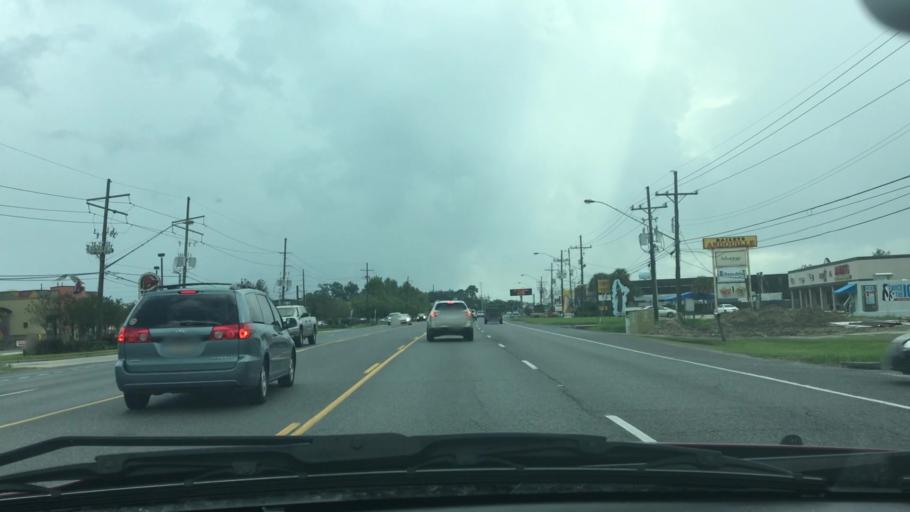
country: US
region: Louisiana
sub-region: Saint John the Baptist Parish
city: Laplace
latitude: 30.0696
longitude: -90.4860
